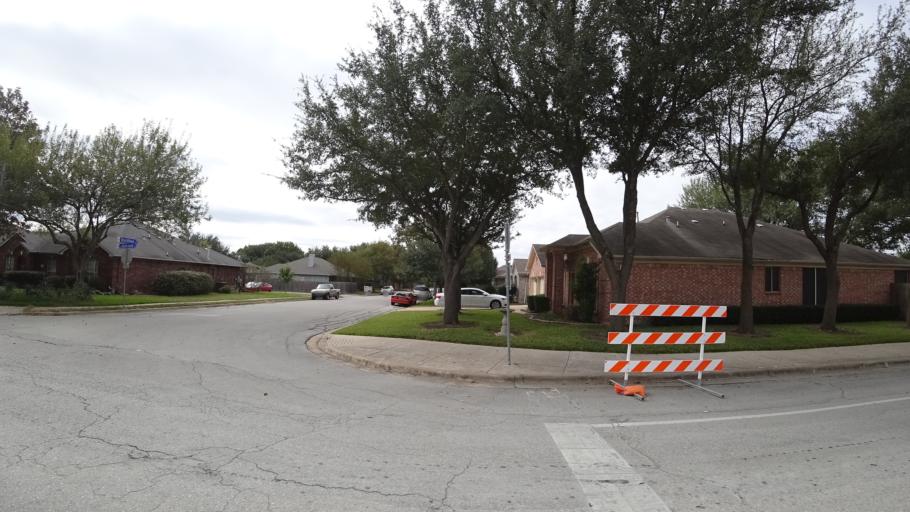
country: US
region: Texas
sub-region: Travis County
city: Windemere
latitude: 30.4625
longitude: -97.6450
